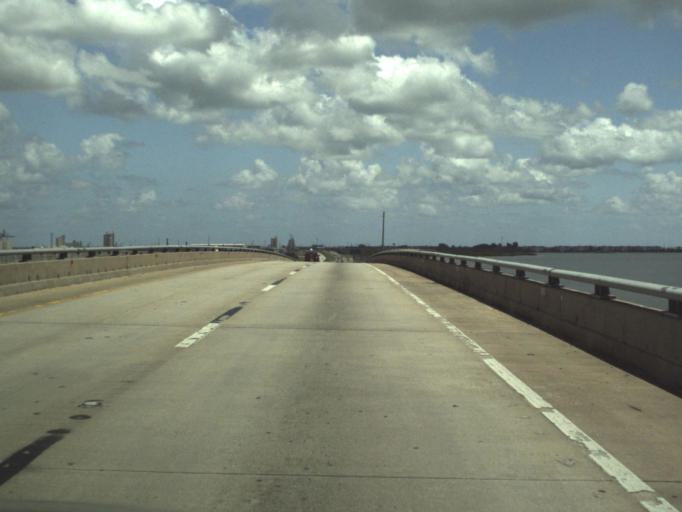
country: US
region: Florida
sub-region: Brevard County
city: Cape Canaveral
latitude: 28.4051
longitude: -80.6457
